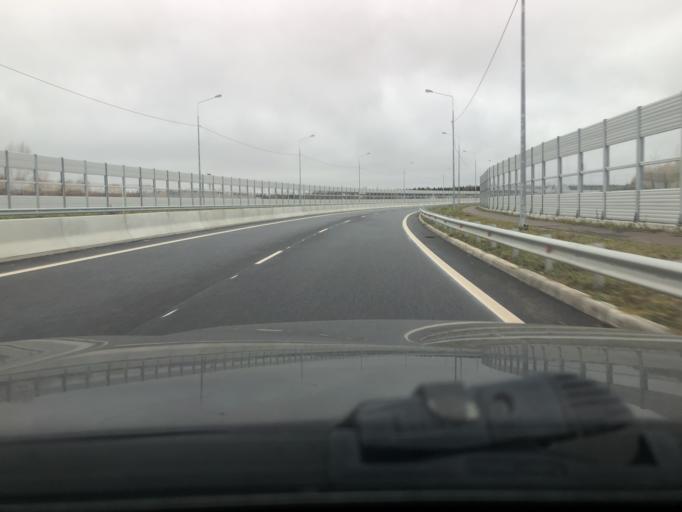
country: RU
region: Moskovskaya
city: Semkhoz
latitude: 56.3210
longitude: 38.0779
